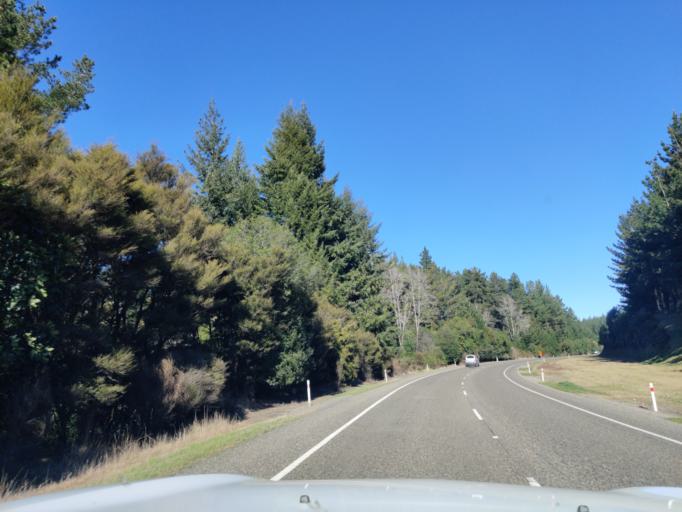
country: NZ
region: Waikato
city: Turangi
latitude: -39.0385
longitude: 175.8159
